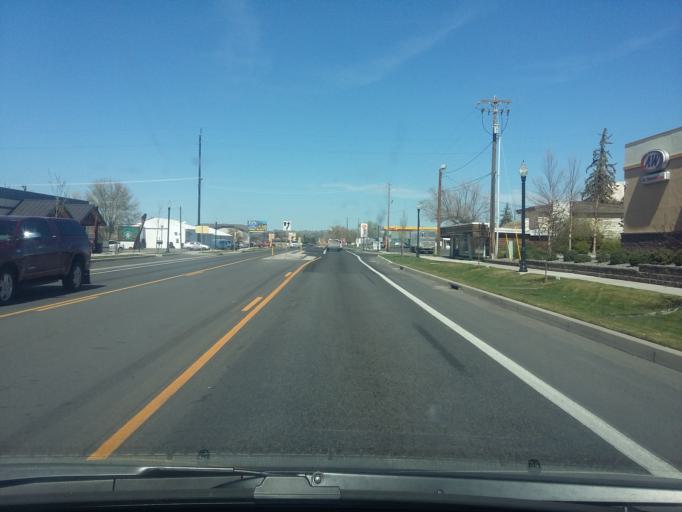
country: US
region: Oregon
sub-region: Jefferson County
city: Madras
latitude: 44.6204
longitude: -121.1323
